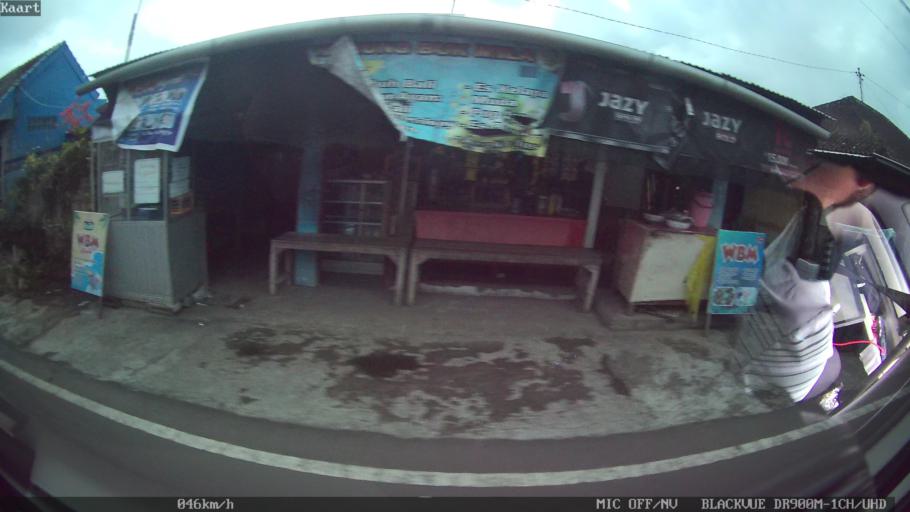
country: ID
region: Bali
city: Petang
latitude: -8.3743
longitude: 115.2237
